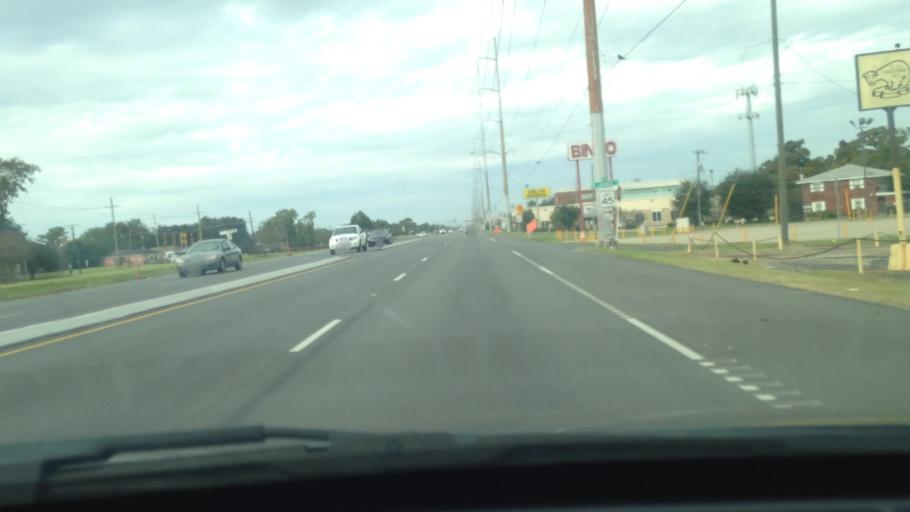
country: US
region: Louisiana
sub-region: Jefferson Parish
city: River Ridge
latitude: 29.9782
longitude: -90.2155
